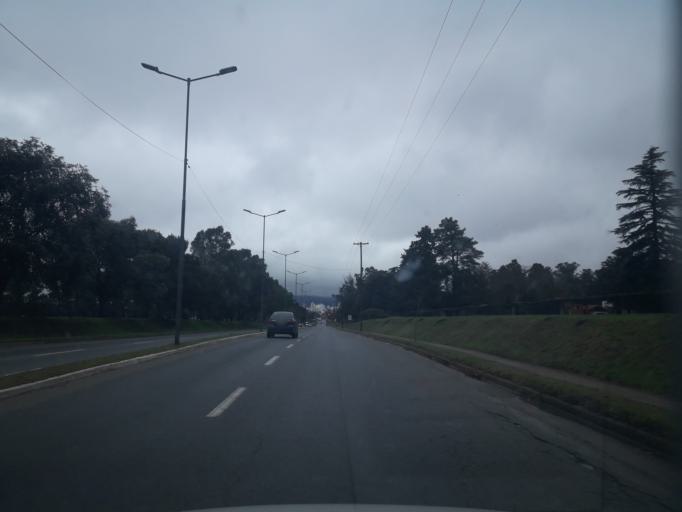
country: AR
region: Buenos Aires
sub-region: Partido de Tandil
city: Tandil
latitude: -37.3065
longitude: -59.1626
